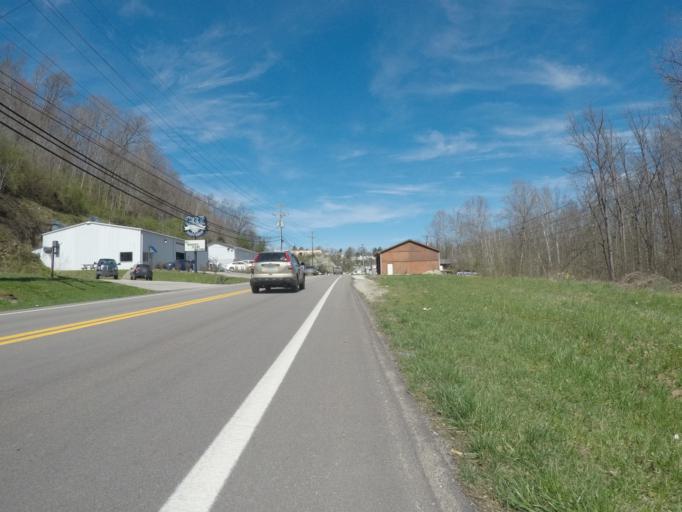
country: US
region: West Virginia
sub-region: Cabell County
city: Pea Ridge
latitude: 38.4068
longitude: -82.3200
